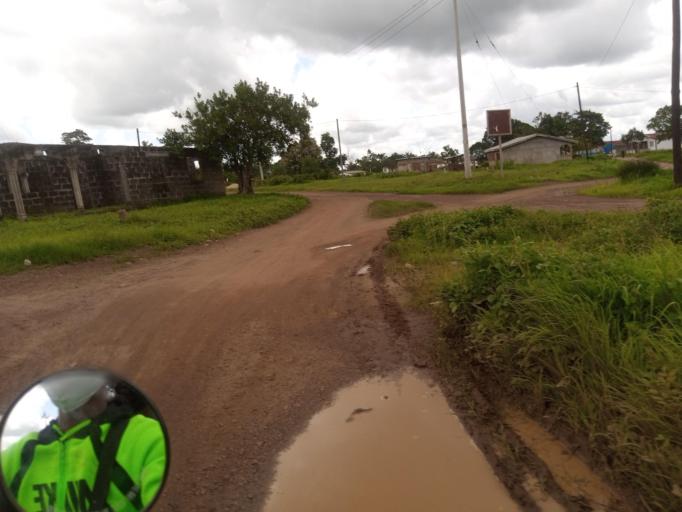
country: SL
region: Northern Province
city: Port Loko
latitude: 8.7657
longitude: -12.7788
